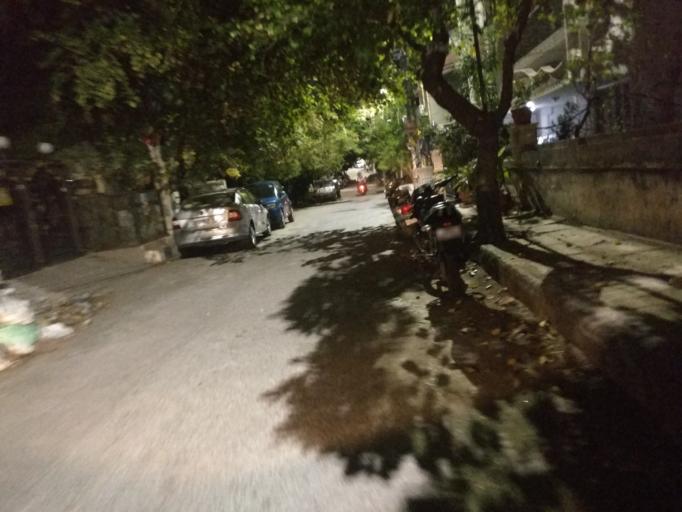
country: IN
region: Telangana
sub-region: Hyderabad
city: Hyderabad
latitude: 17.4136
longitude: 78.4526
